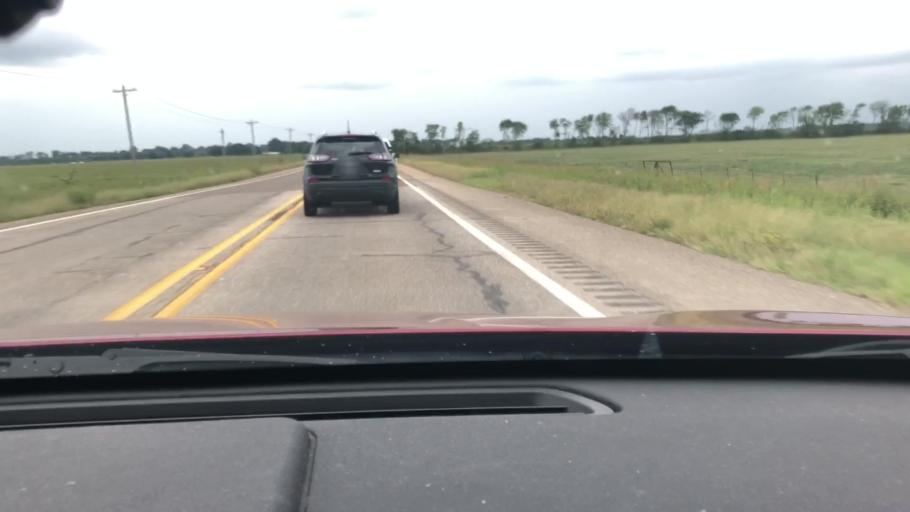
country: US
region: Arkansas
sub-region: Lafayette County
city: Lewisville
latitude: 33.3850
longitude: -93.7361
